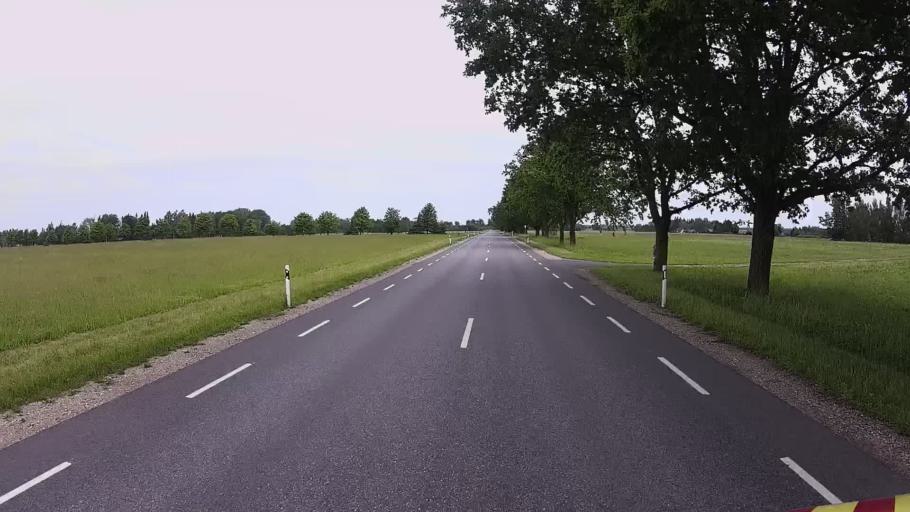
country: EE
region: Viljandimaa
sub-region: Karksi vald
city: Karksi-Nuia
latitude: 58.1241
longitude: 25.5826
